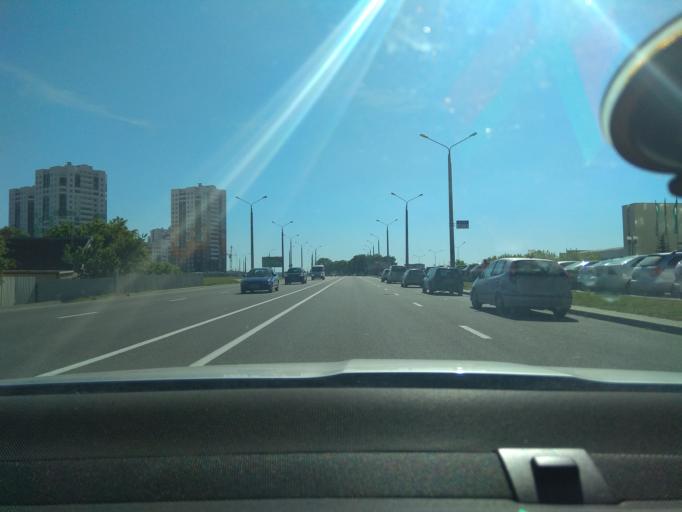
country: BY
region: Grodnenskaya
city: Hrodna
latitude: 53.6507
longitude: 23.7864
